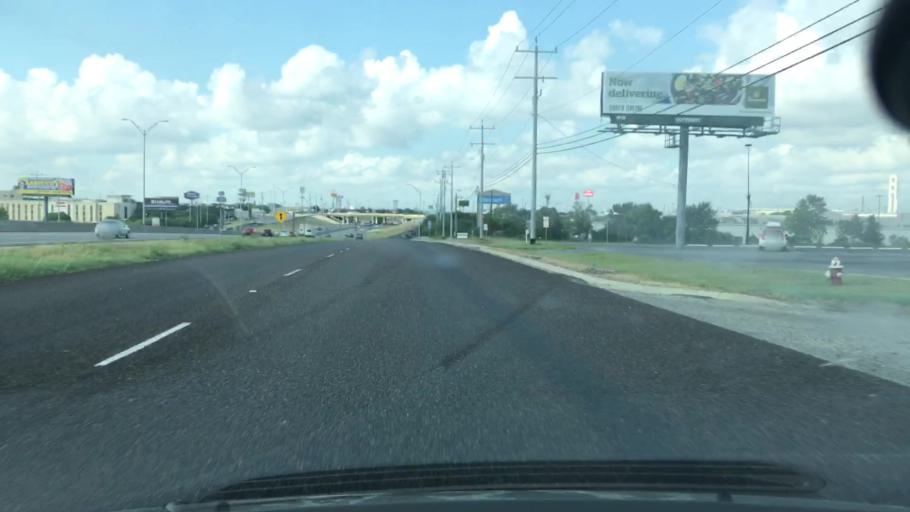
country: US
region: Texas
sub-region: Bexar County
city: Selma
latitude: 29.6047
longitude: -98.2723
